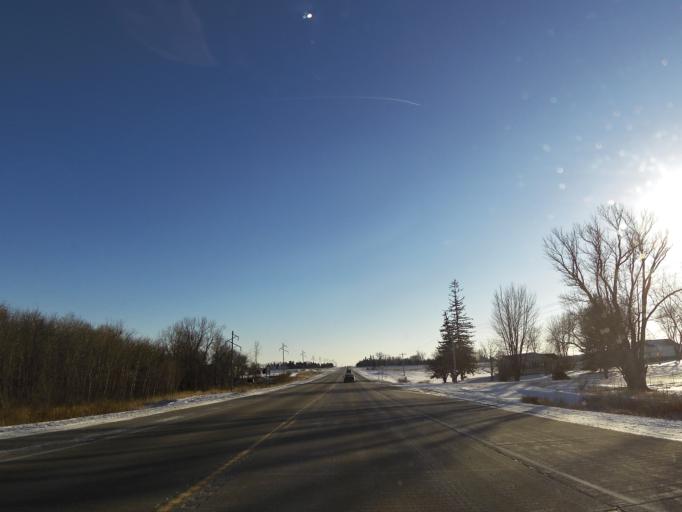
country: US
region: Minnesota
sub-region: Le Sueur County
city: New Prague
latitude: 44.5261
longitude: -93.5856
